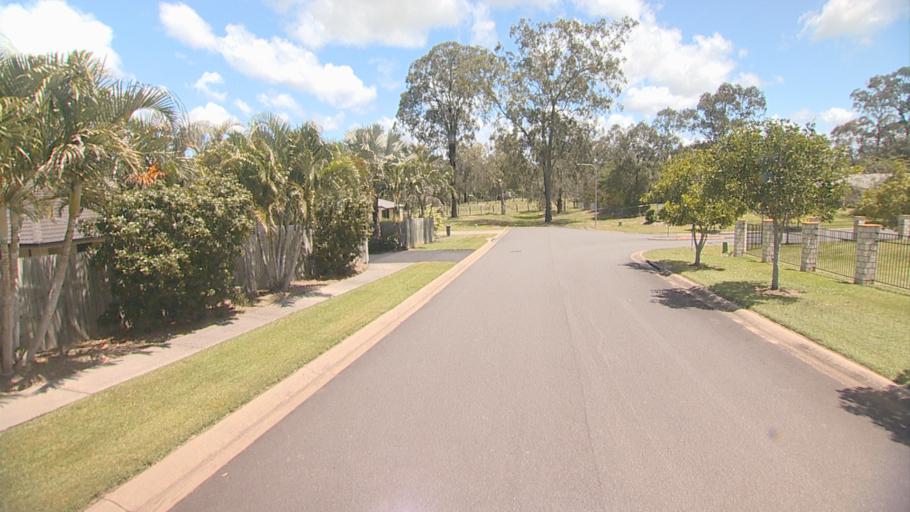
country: AU
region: Queensland
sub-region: Gold Coast
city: Yatala
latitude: -27.6678
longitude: 153.2303
